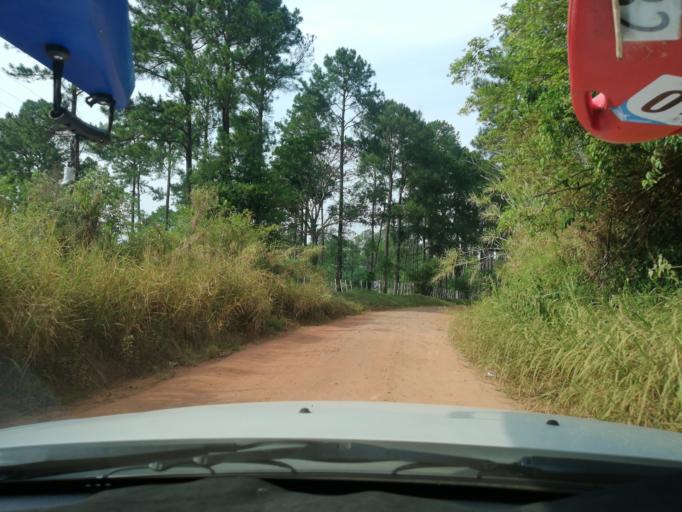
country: AR
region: Misiones
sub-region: Departamento de San Ignacio
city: San Ignacio
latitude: -27.2915
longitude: -55.5630
